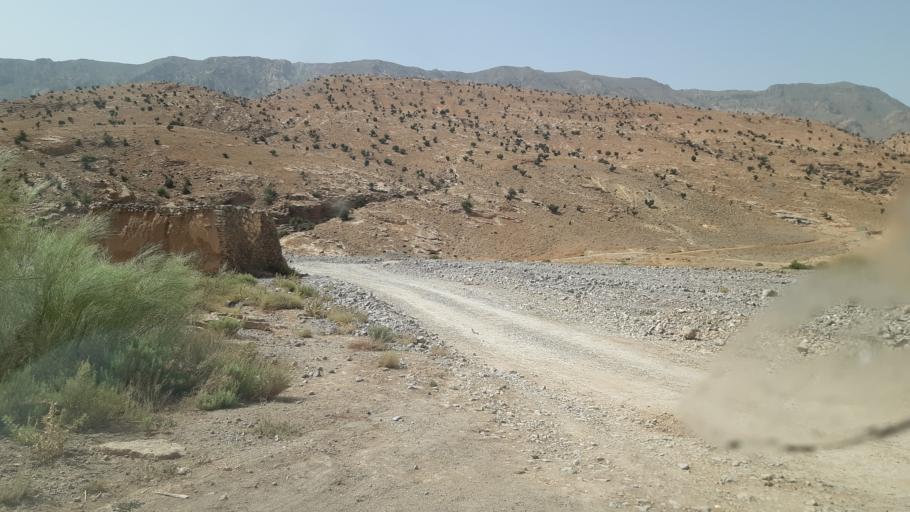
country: MA
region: Meknes-Tafilalet
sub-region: Khenifra
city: Midelt
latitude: 32.5837
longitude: -4.7672
